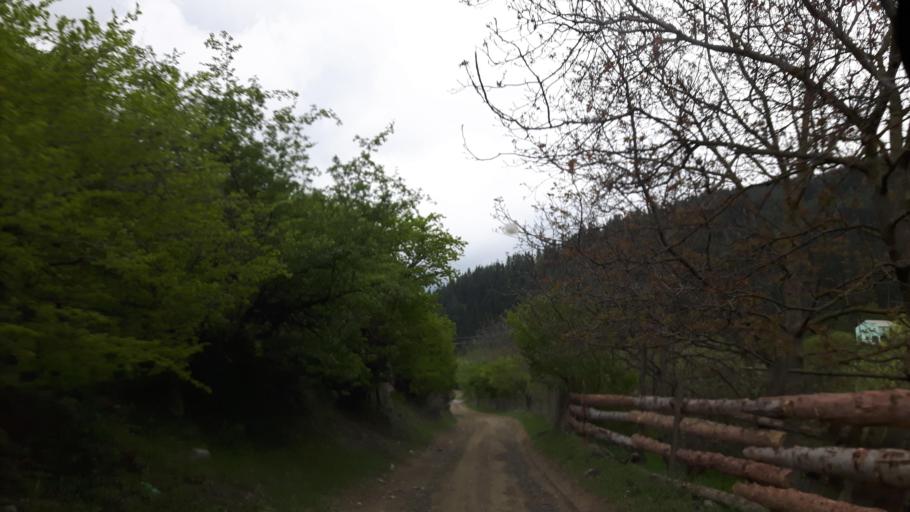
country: GE
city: Agara
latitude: 41.8634
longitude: 43.9249
